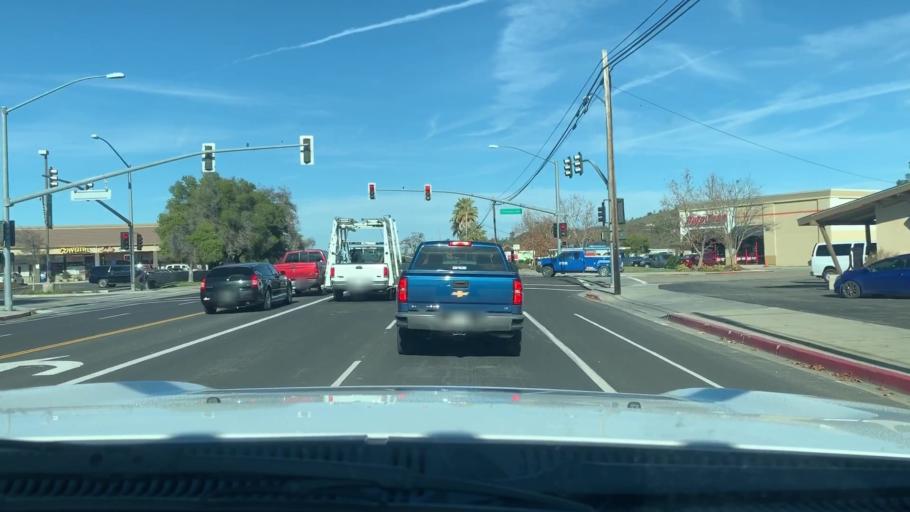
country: US
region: California
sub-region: San Luis Obispo County
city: Atascadero
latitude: 35.4745
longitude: -120.6545
